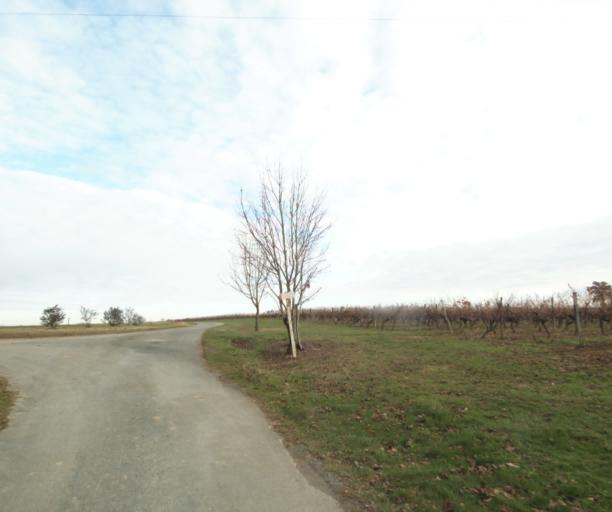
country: FR
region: Poitou-Charentes
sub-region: Departement de la Charente-Maritime
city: Corme-Royal
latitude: 45.7443
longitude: -0.7987
